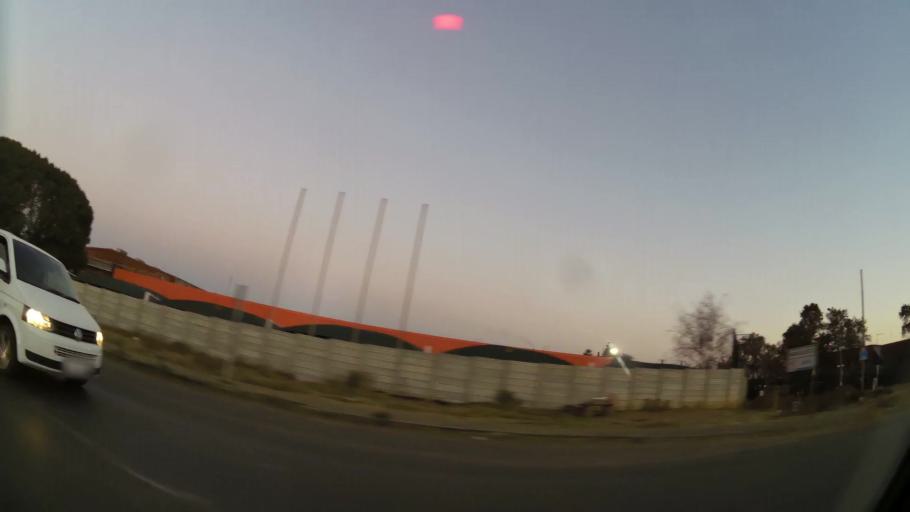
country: ZA
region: Gauteng
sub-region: Ekurhuleni Metropolitan Municipality
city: Germiston
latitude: -26.2750
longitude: 28.1714
